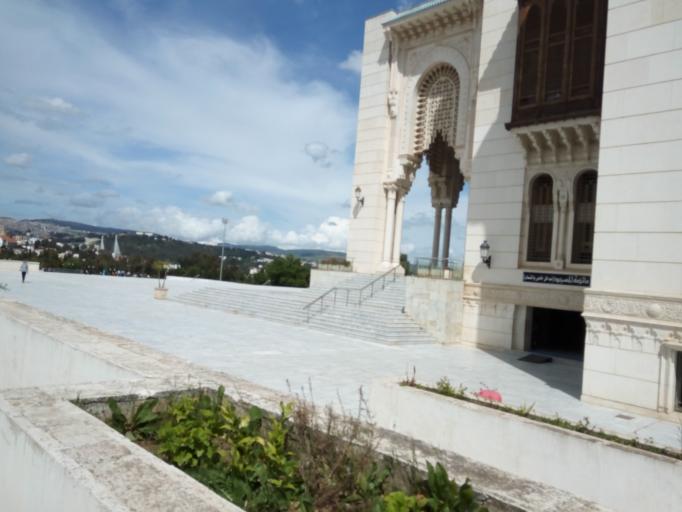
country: DZ
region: Constantine
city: Constantine
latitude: 36.3474
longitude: 6.6028
